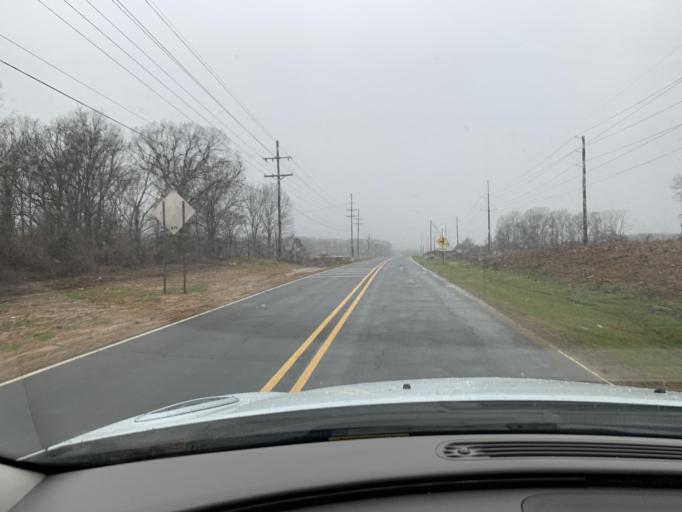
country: US
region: Mississippi
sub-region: De Soto County
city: Hernando
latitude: 34.8605
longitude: -89.9705
